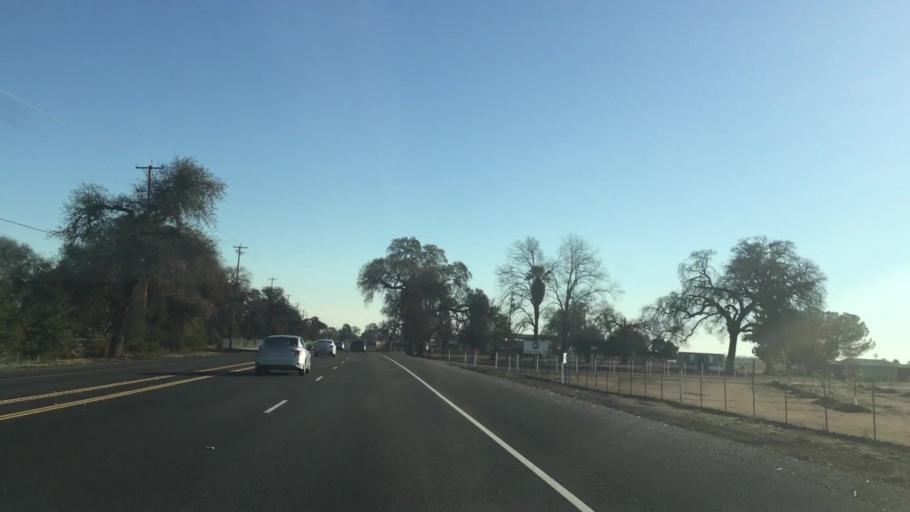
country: US
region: California
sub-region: Butte County
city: Gridley
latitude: 39.3566
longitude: -121.6047
